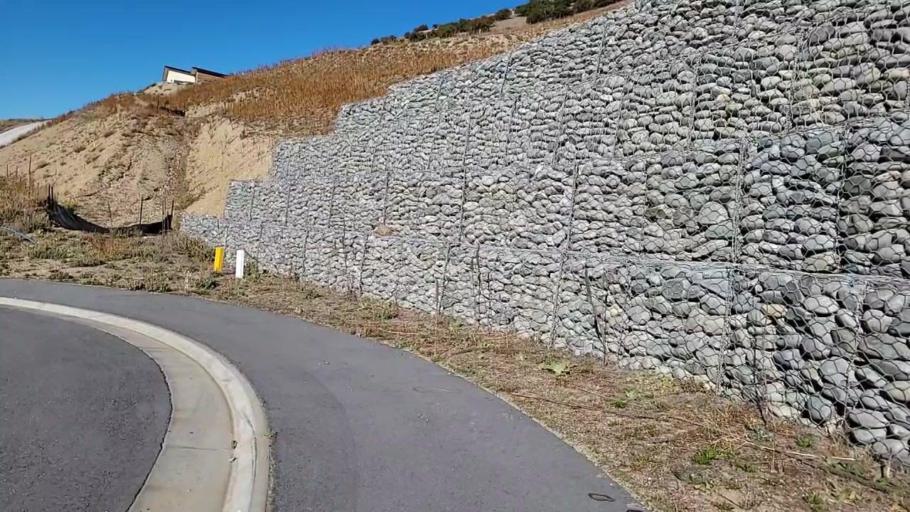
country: NZ
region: Otago
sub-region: Queenstown-Lakes District
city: Wanaka
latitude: -44.9980
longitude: 169.2058
